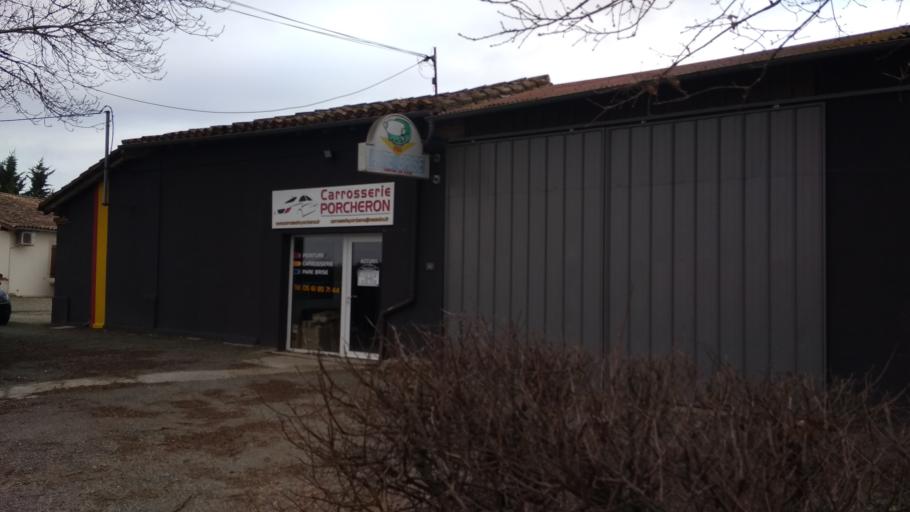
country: FR
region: Midi-Pyrenees
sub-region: Departement du Gers
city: Pujaudran
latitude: 43.6478
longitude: 1.1114
